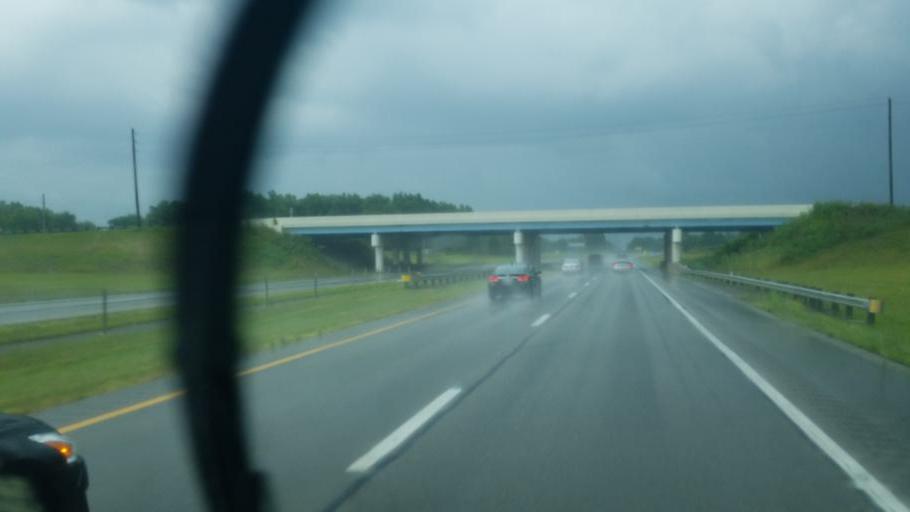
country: US
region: Ohio
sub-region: Trumbull County
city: Morgandale
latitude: 41.2771
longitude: -80.8029
